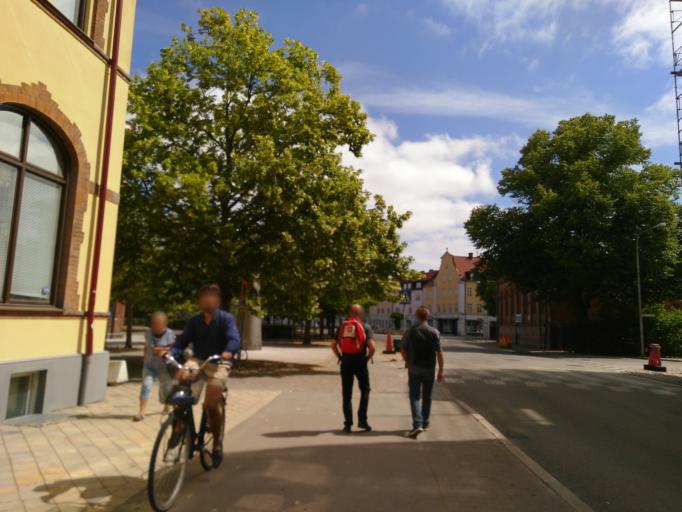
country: SE
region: Skane
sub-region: Landskrona
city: Landskrona
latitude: 55.8716
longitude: 12.8344
